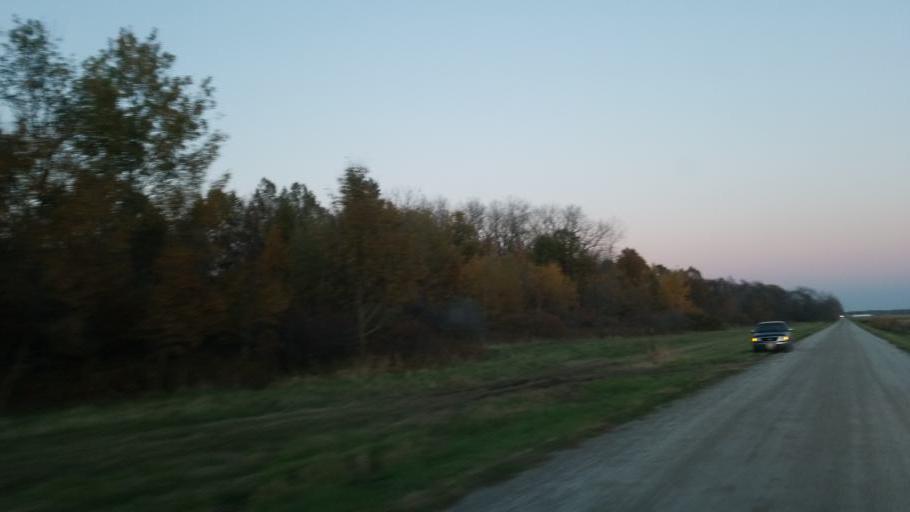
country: US
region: Ohio
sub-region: Huron County
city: Willard
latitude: 40.9959
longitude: -82.7759
